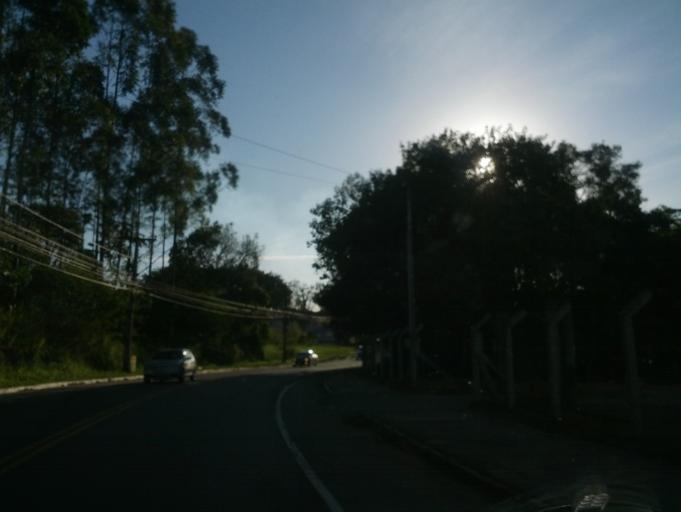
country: BR
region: Santa Catarina
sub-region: Indaial
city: Indaial
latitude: -26.8893
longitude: -49.2033
